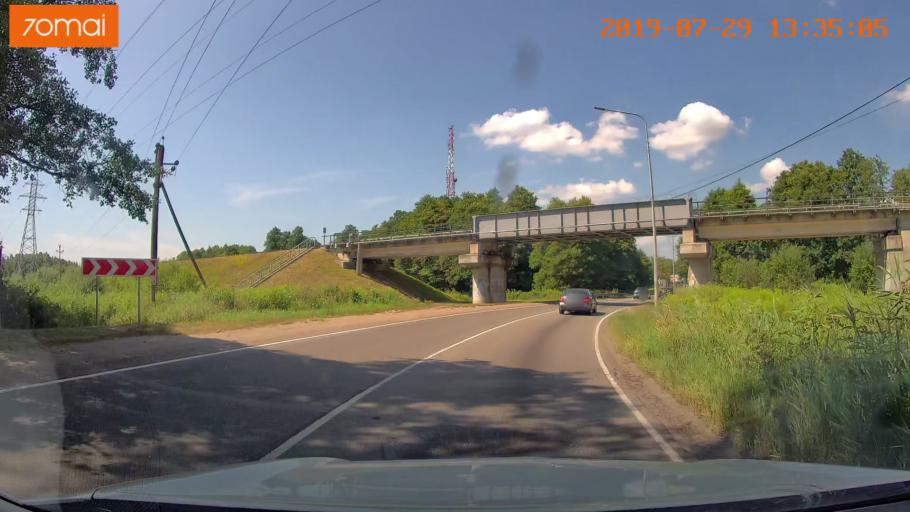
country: RU
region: Kaliningrad
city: Volochayevskoye
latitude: 54.6992
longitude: 20.2094
